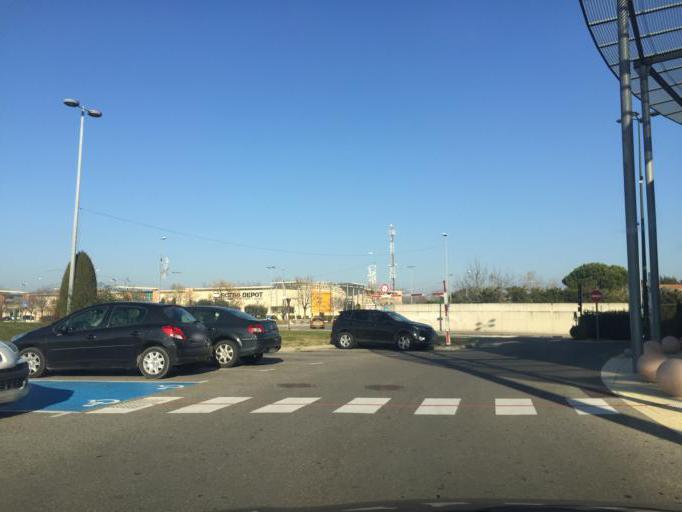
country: FR
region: Provence-Alpes-Cote d'Azur
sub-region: Departement du Vaucluse
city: Montfavet
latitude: 43.9210
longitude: 4.8676
